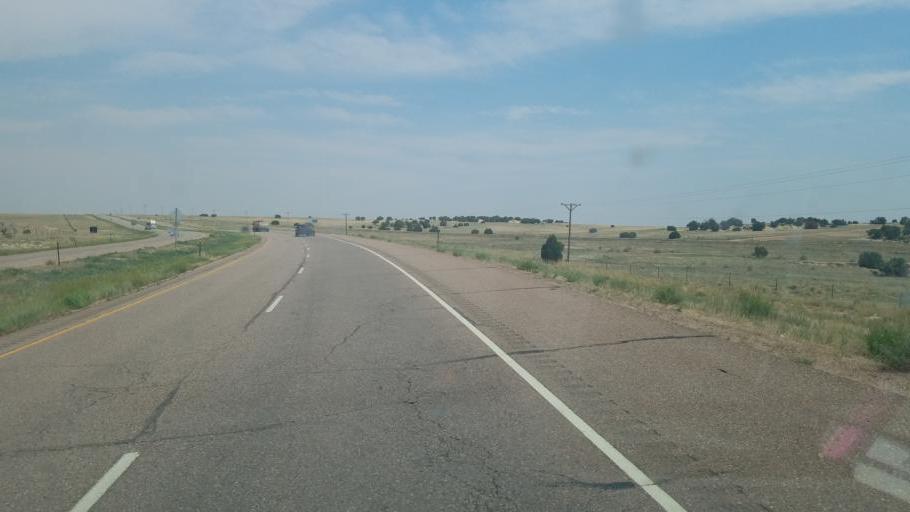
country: US
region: Colorado
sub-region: Fremont County
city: Penrose
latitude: 38.3730
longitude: -104.9429
